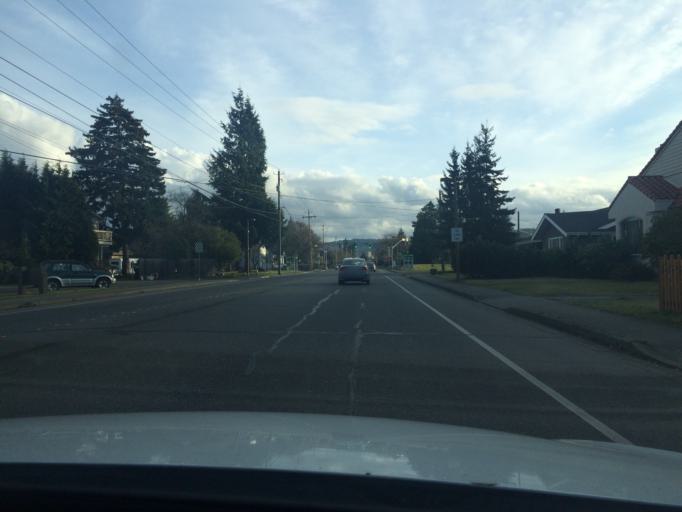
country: US
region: Washington
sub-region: Whatcom County
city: Bellingham
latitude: 48.7695
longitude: -122.4922
